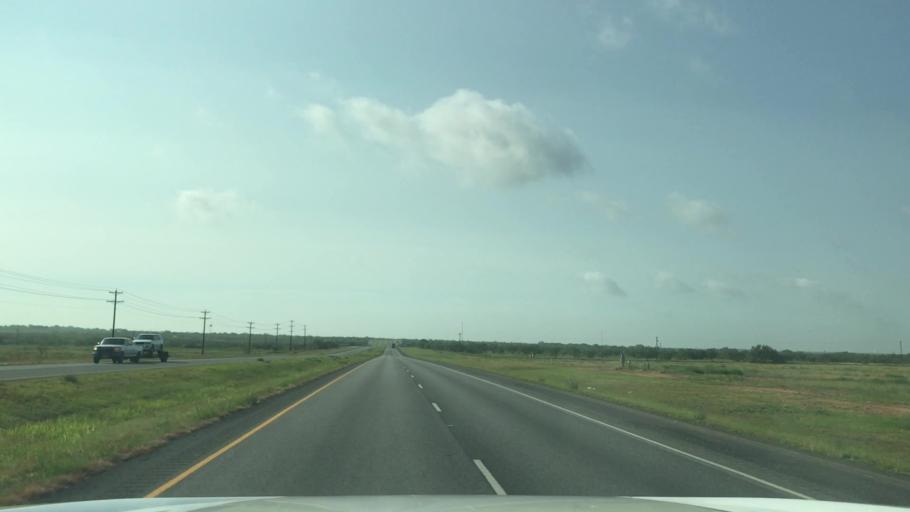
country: US
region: Texas
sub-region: Scurry County
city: Snyder
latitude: 32.7741
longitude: -100.9406
